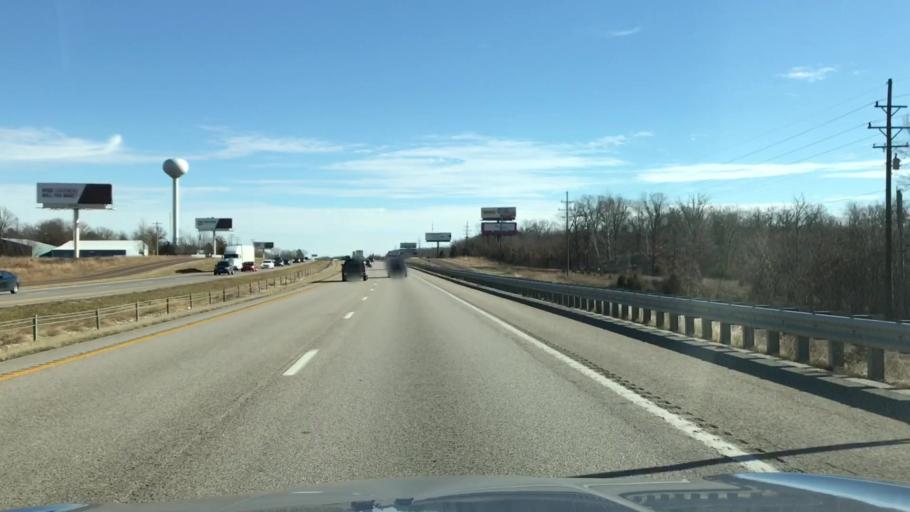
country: US
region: Missouri
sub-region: Warren County
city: Warrenton
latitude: 38.8269
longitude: -91.2077
